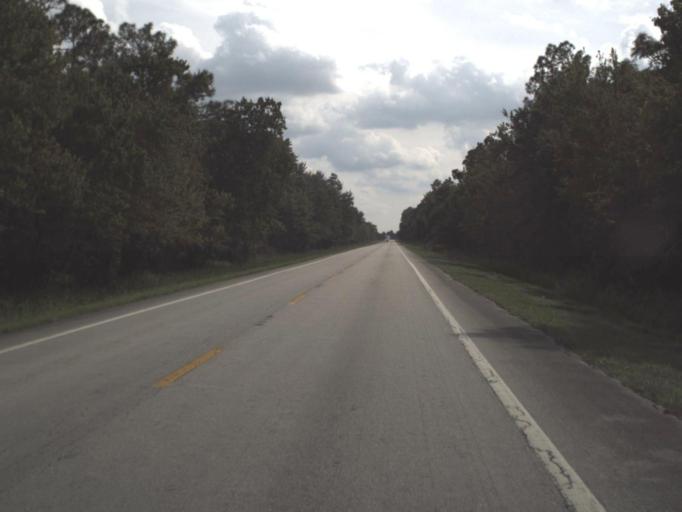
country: US
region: Florida
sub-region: Okeechobee County
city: Cypress Quarters
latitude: 27.5121
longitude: -80.8071
